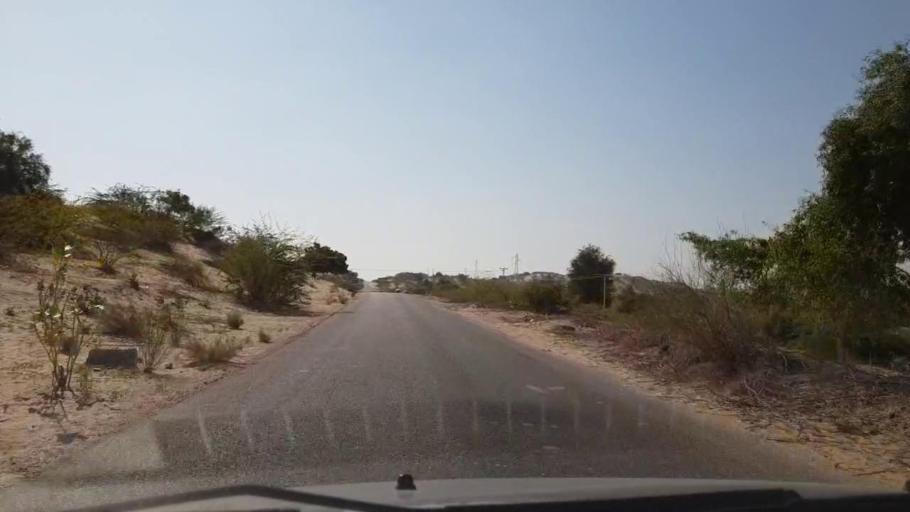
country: PK
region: Sindh
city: Diplo
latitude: 24.5707
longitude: 69.6819
